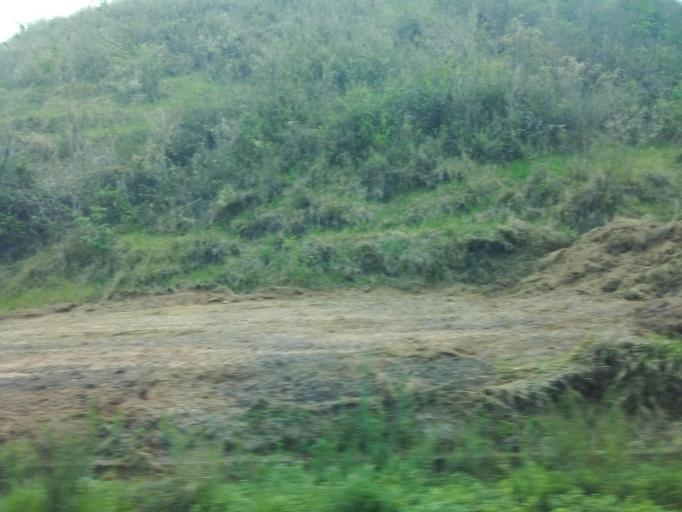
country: BR
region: Minas Gerais
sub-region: Governador Valadares
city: Governador Valadares
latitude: -19.0975
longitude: -42.1664
